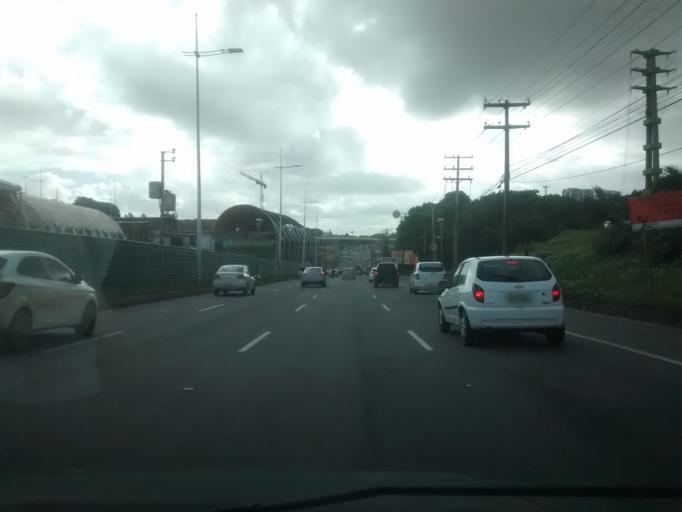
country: BR
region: Bahia
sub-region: Salvador
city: Salvador
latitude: -12.9481
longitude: -38.4228
